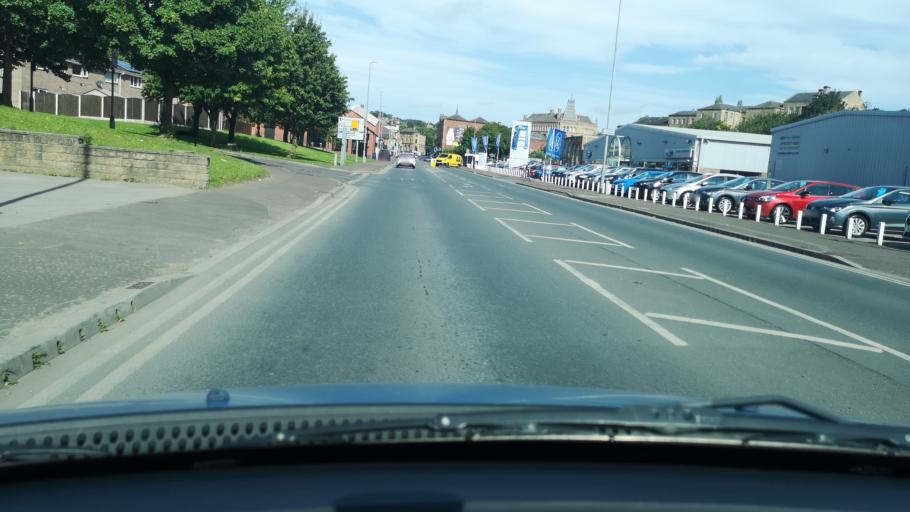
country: GB
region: England
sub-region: Kirklees
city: Batley
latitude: 53.7083
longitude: -1.6268
